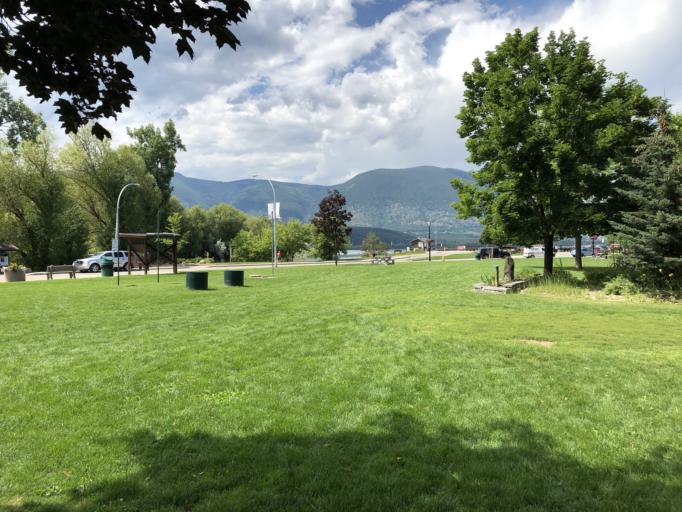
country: CA
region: British Columbia
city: Salmon Arm
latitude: 50.7064
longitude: -119.2821
